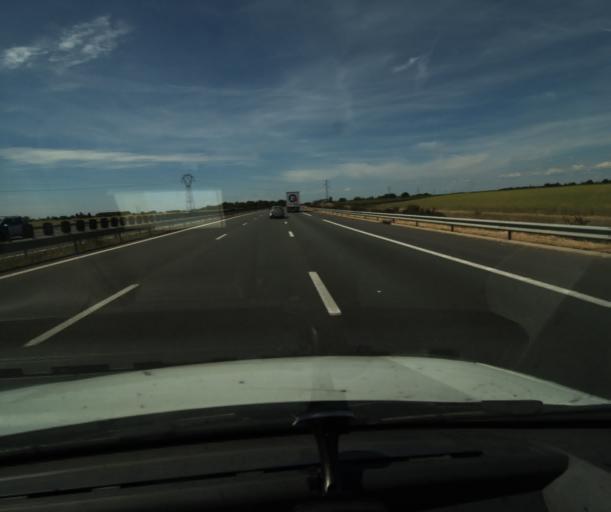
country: FR
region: Midi-Pyrenees
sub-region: Departement du Tarn-et-Garonne
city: Grisolles
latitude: 43.8509
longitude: 1.3201
